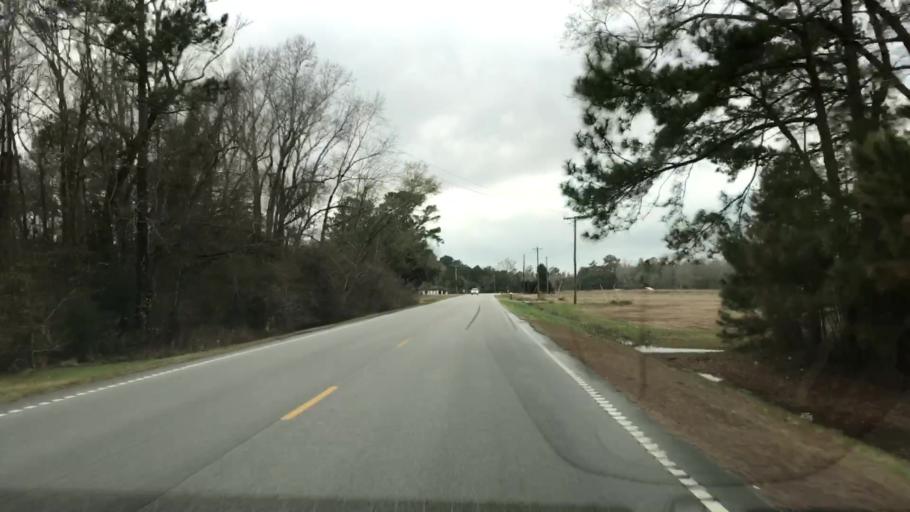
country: US
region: South Carolina
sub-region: Berkeley County
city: Saint Stephen
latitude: 33.2822
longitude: -79.7252
